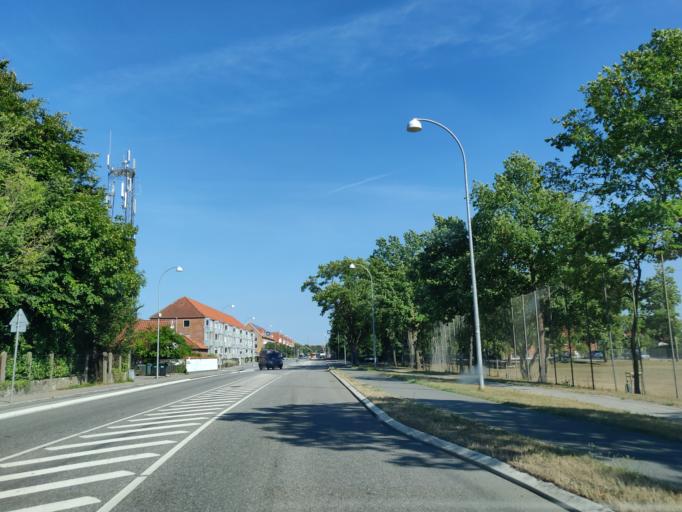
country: DK
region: Zealand
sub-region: Roskilde Kommune
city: Roskilde
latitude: 55.6354
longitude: 12.0586
